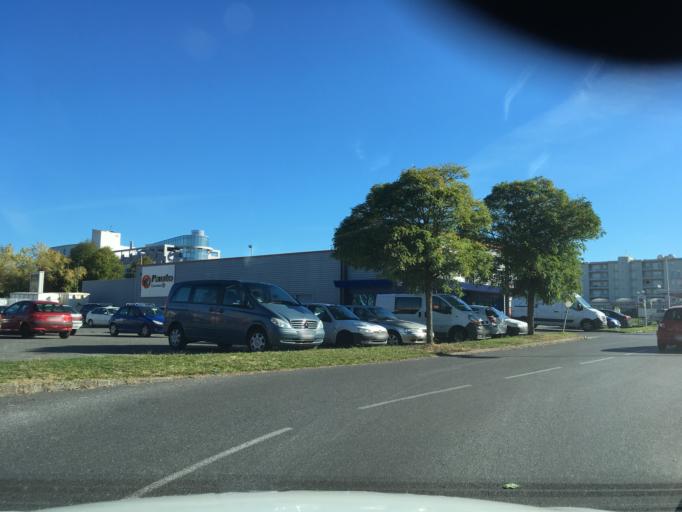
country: FR
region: Aquitaine
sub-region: Departement des Pyrenees-Atlantiques
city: Pau
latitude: 43.3176
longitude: -0.3580
